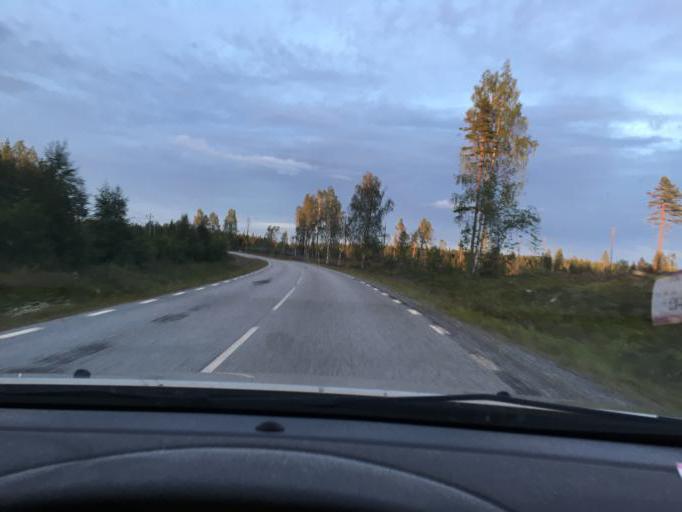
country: SE
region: Norrbotten
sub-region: Lulea Kommun
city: Ranea
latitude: 66.0496
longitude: 22.3953
